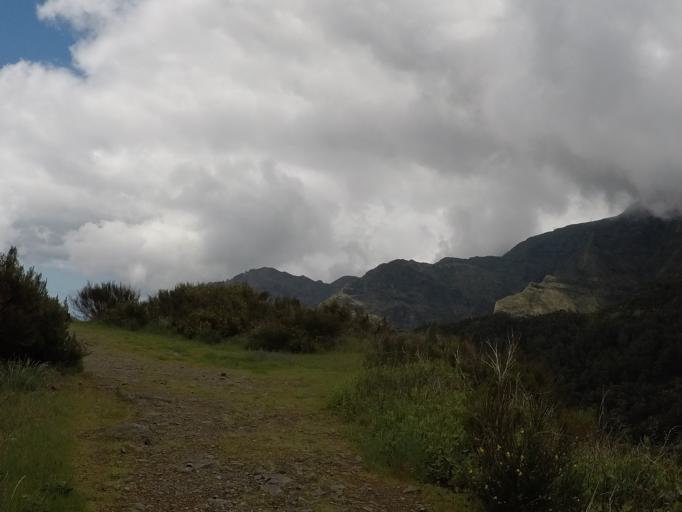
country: PT
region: Madeira
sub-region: Sao Vicente
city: Sao Vicente
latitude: 32.7494
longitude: -17.0177
